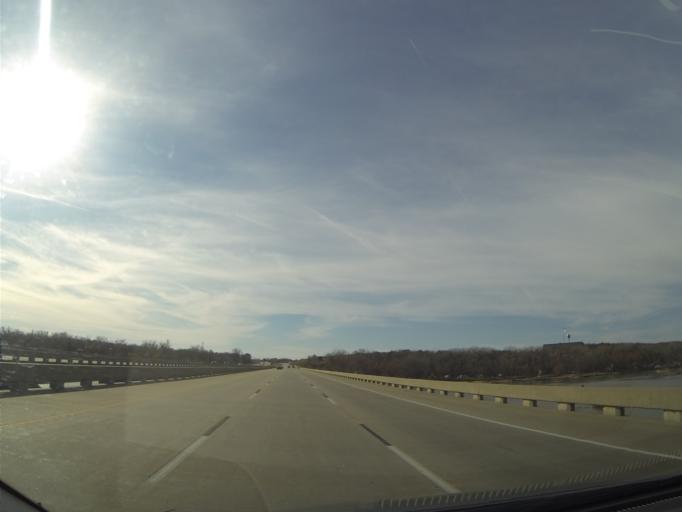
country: US
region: Nebraska
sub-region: Saunders County
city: Ashland
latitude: 41.0282
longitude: -96.2960
